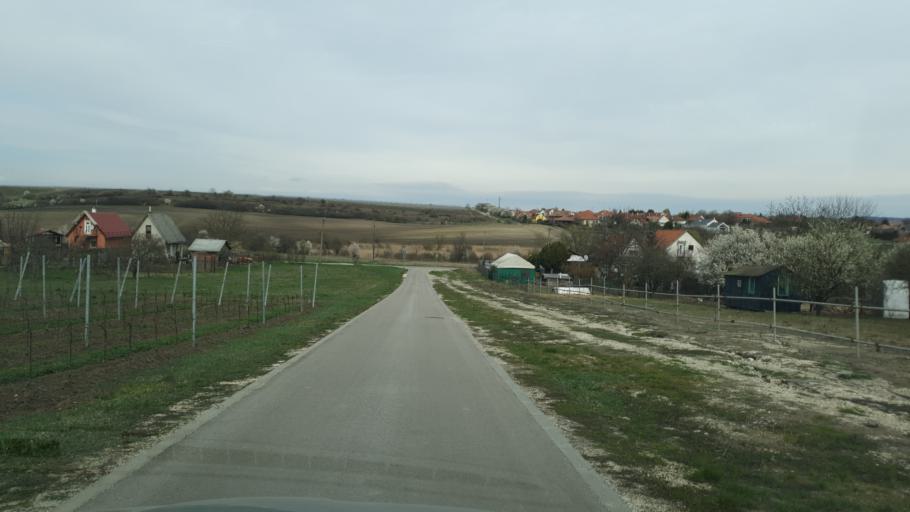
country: HU
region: Fejer
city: Etyek
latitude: 47.4497
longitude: 18.7378
